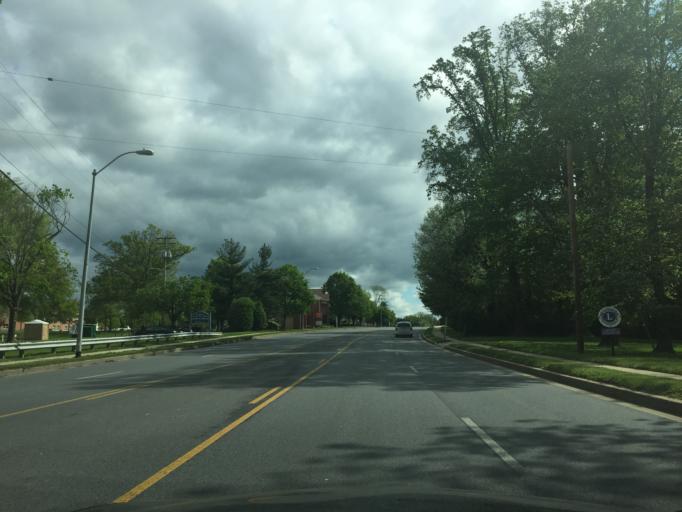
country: US
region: Maryland
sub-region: Baltimore County
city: Reisterstown
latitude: 39.4449
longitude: -76.8172
